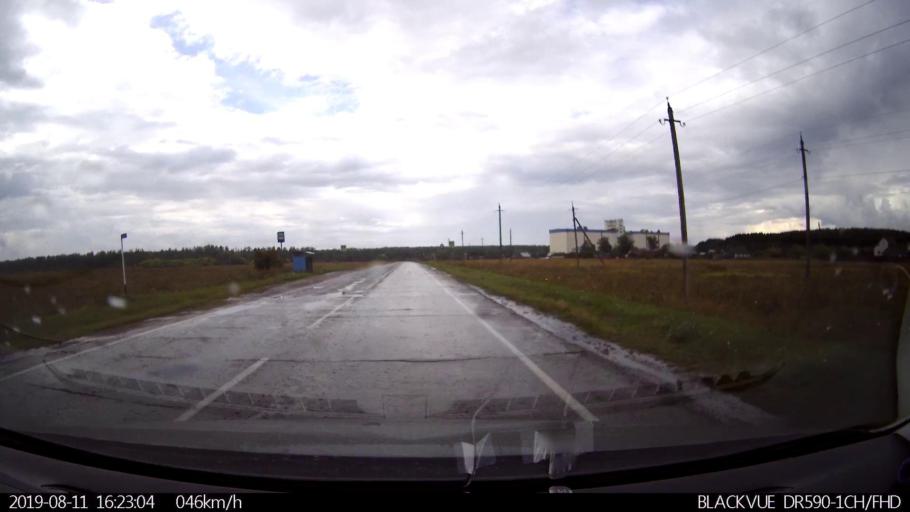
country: RU
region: Ulyanovsk
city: Mayna
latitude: 54.0926
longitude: 47.5901
